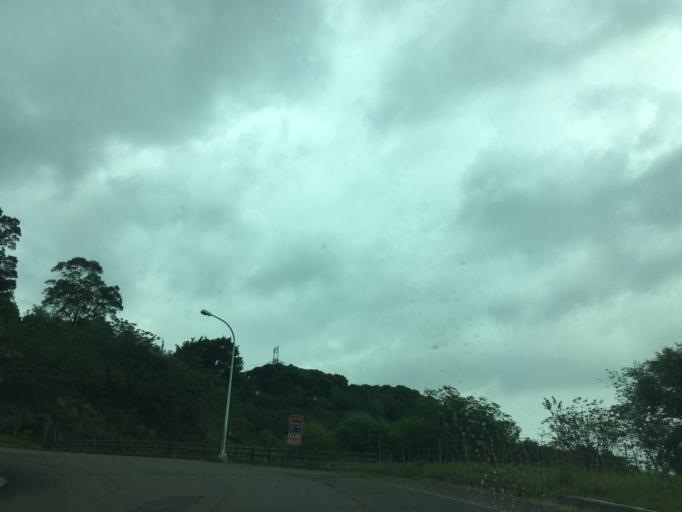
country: TW
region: Taiwan
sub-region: Taichung City
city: Taichung
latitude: 24.0651
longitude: 120.7187
